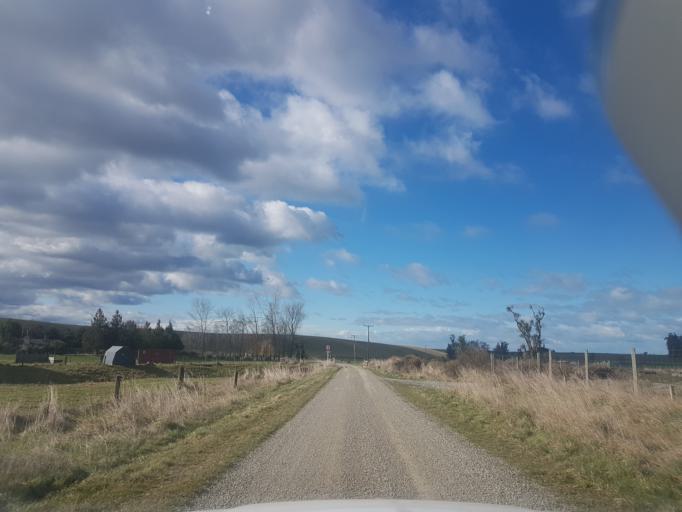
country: NZ
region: Canterbury
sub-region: Timaru District
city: Pleasant Point
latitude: -44.1885
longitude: 171.1824
